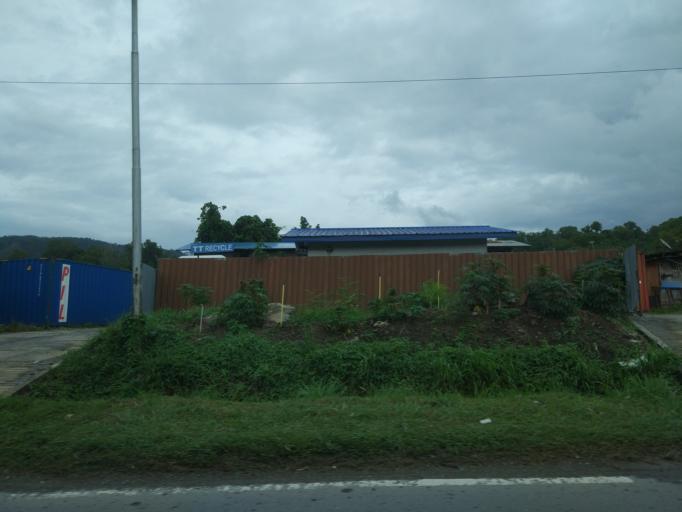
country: MY
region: Sabah
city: Kota Kinabalu
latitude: 6.0979
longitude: 116.2016
